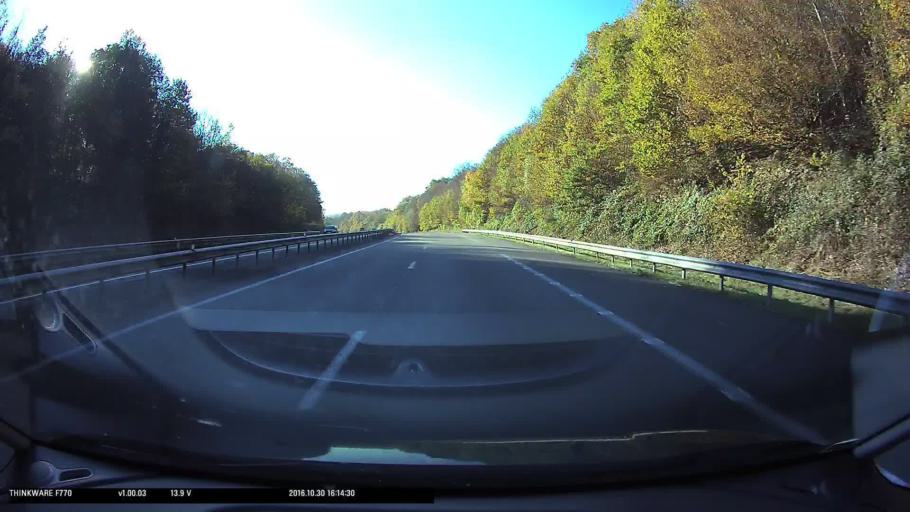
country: FR
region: Franche-Comte
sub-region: Departement du Doubs
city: Clerval
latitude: 47.4198
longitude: 6.5938
